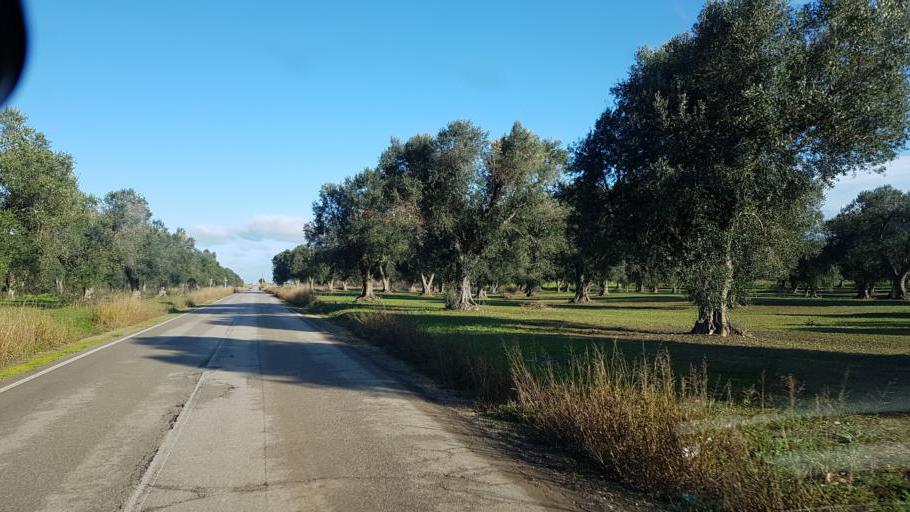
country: IT
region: Apulia
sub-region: Provincia di Brindisi
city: Tuturano
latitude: 40.5646
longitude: 17.9490
